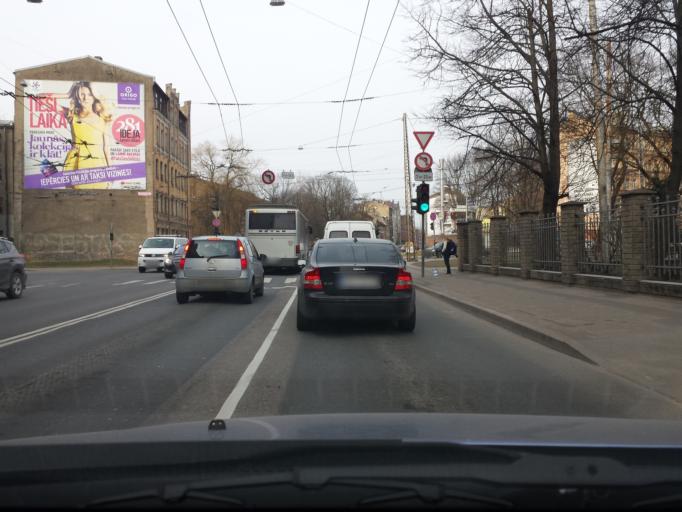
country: LV
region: Riga
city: Riga
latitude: 56.9416
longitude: 24.1306
